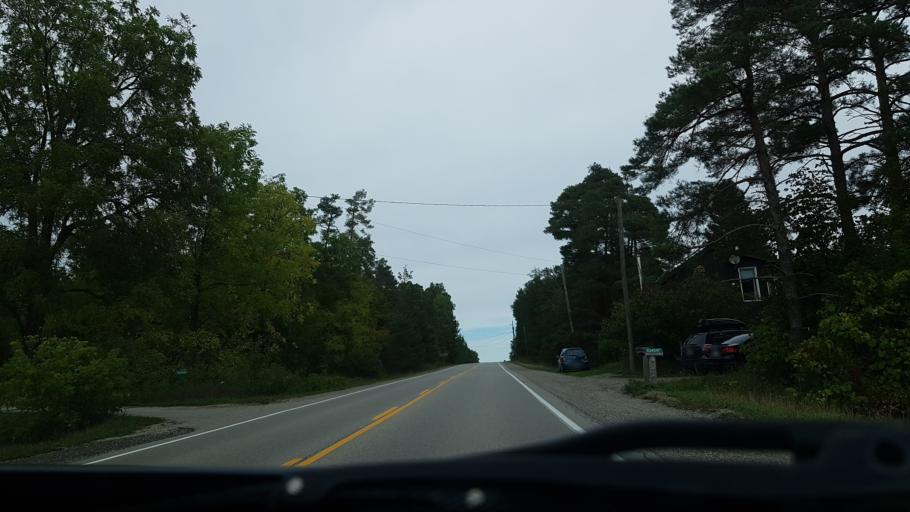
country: CA
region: Ontario
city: Orangeville
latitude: 44.0079
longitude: -80.0006
